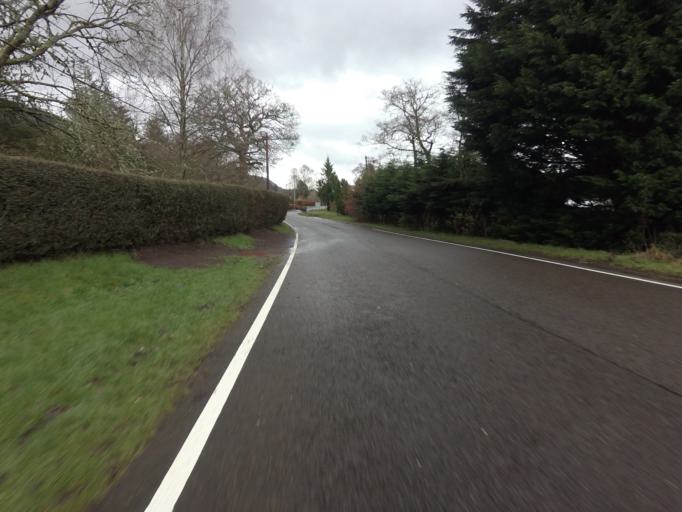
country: GB
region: Scotland
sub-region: Stirling
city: Killearn
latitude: 56.1880
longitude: -4.4818
